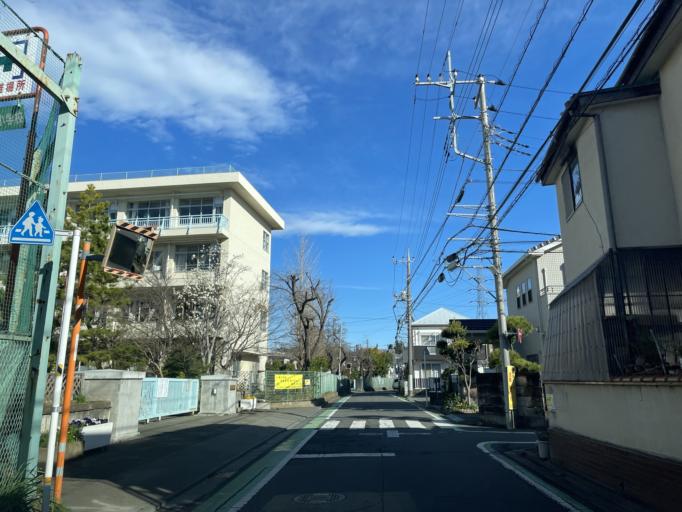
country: JP
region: Saitama
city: Tokorozawa
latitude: 35.7833
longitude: 139.4489
